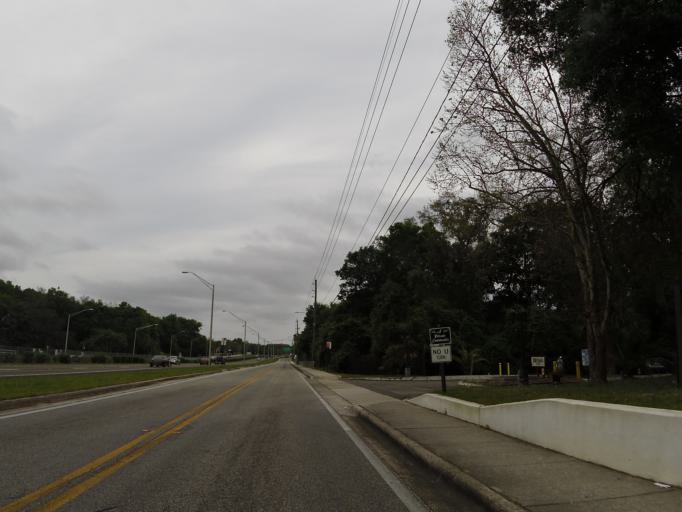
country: US
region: Florida
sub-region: Duval County
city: Jacksonville
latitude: 30.3273
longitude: -81.5777
